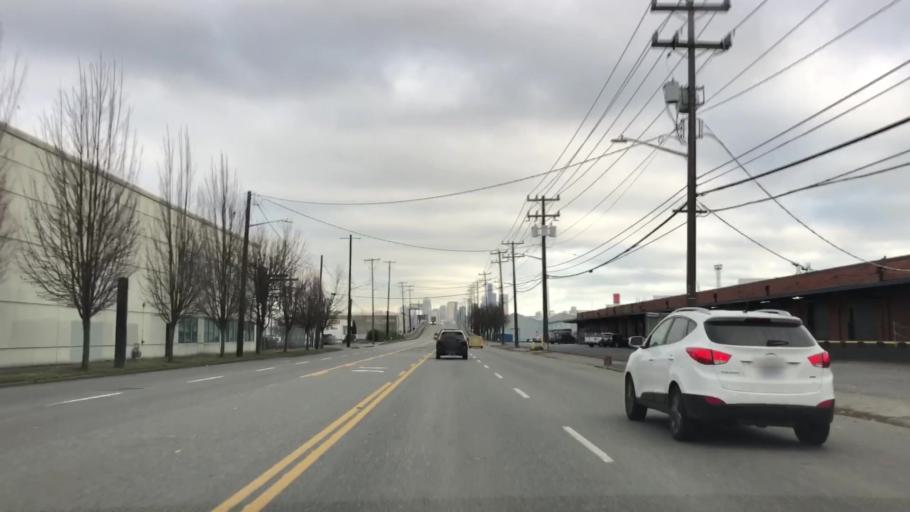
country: US
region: Washington
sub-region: King County
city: White Center
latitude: 47.5577
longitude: -122.3342
